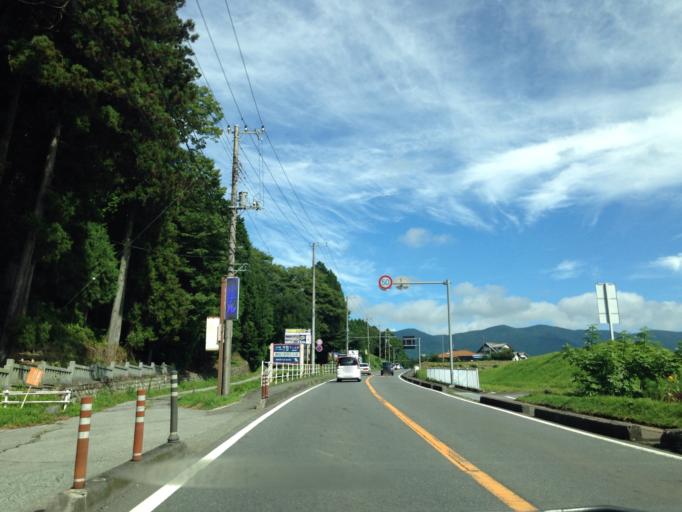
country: JP
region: Shizuoka
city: Gotemba
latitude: 35.3251
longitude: 138.9082
